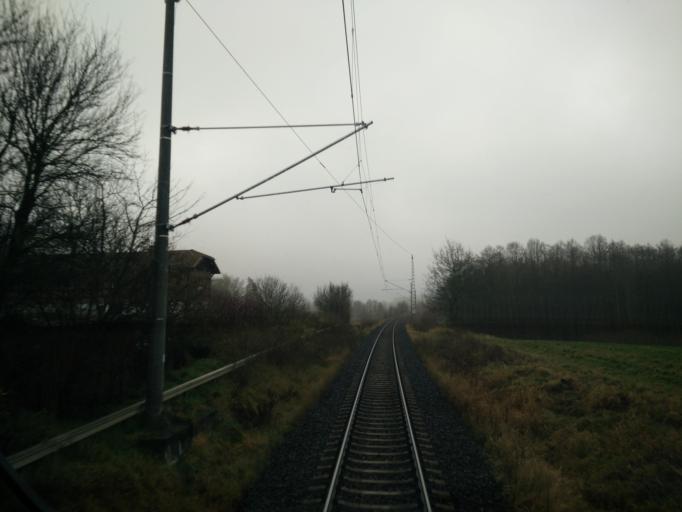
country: DE
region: Mecklenburg-Vorpommern
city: Mecklenburg
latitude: 53.8368
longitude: 11.4769
